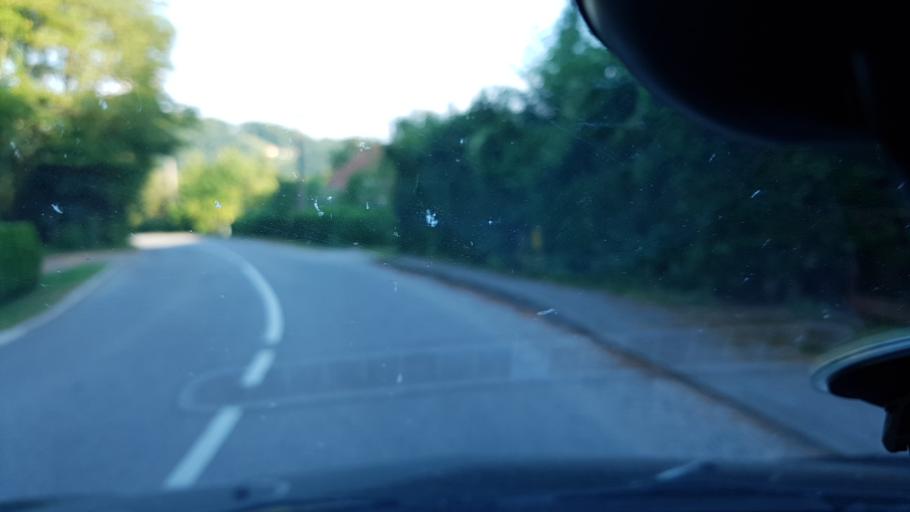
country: SI
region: Bistrica ob Sotli
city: Bistrica ob Sotli
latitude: 46.0513
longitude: 15.7465
